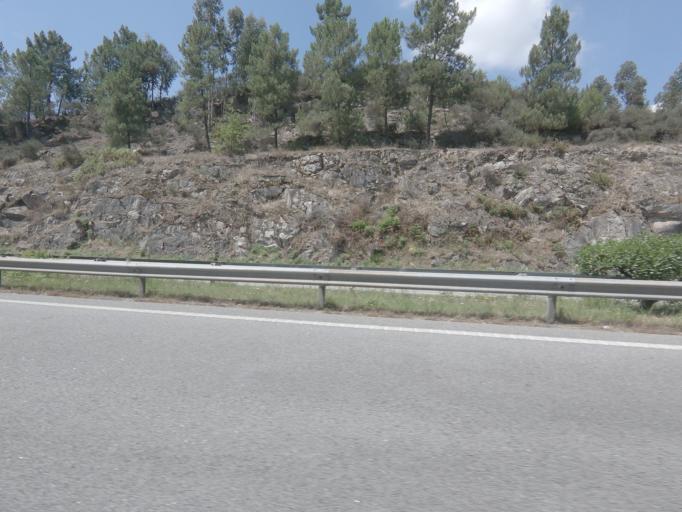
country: PT
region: Porto
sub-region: Paredes
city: Baltar
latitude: 41.1797
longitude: -8.3770
